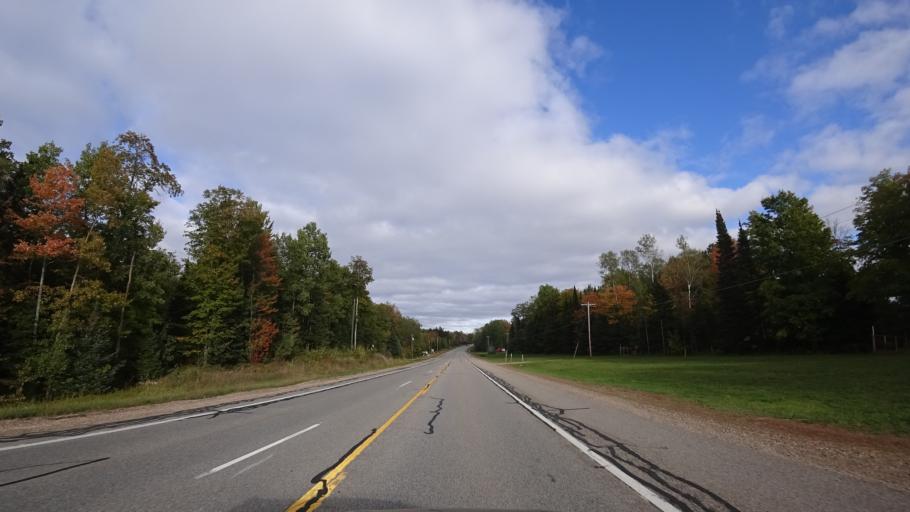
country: US
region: Michigan
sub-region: Alger County
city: Munising
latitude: 46.4416
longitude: -86.7459
